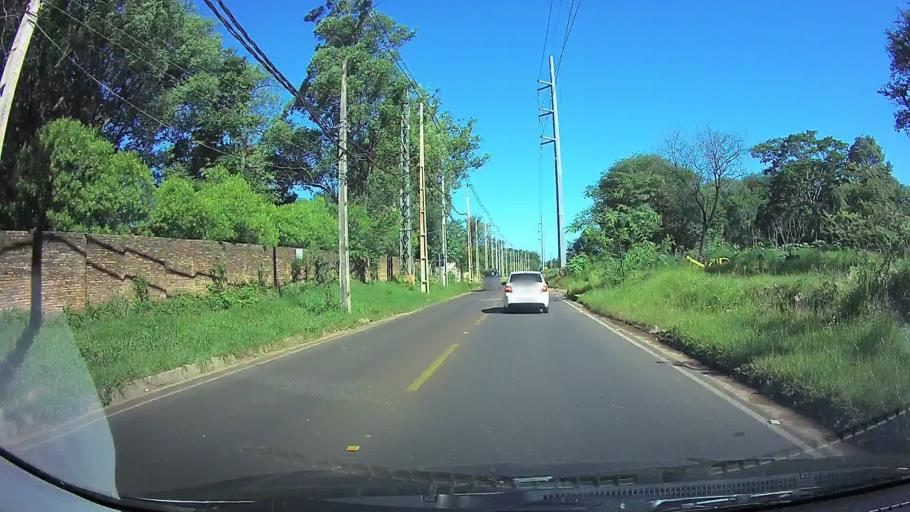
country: PY
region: Central
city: Fernando de la Mora
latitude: -25.3195
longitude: -57.5170
